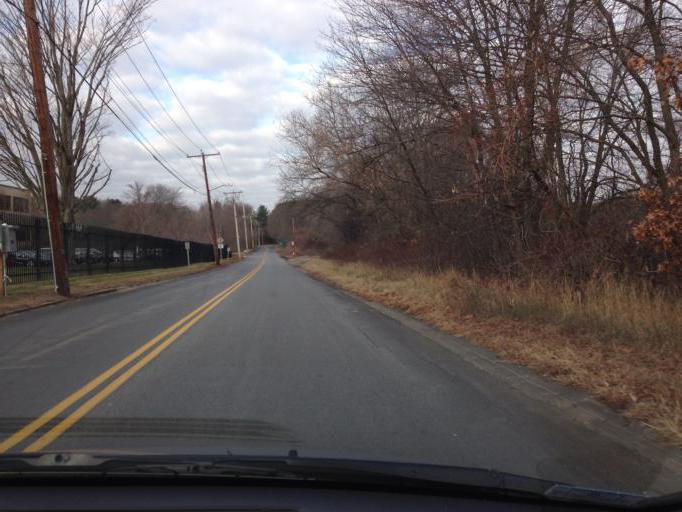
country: US
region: Massachusetts
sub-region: Middlesex County
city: Bedford
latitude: 42.4780
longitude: -71.2949
